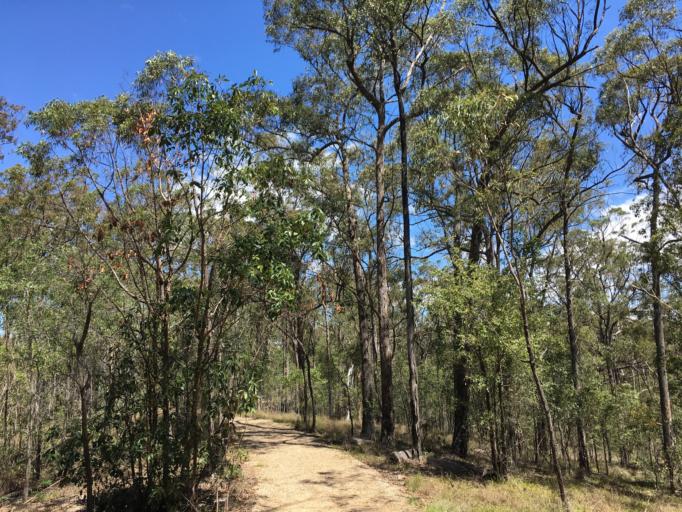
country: AU
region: Queensland
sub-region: Logan
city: Woodridge
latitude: -27.6256
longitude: 153.0903
